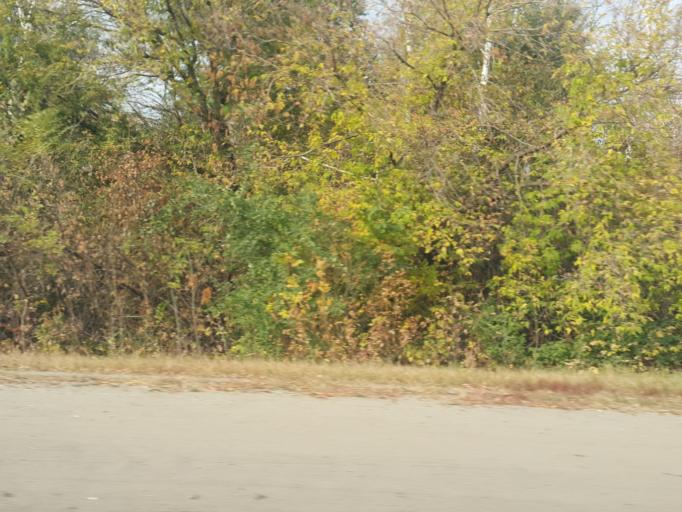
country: RU
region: Tambov
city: Bokino
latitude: 52.6659
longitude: 41.4504
